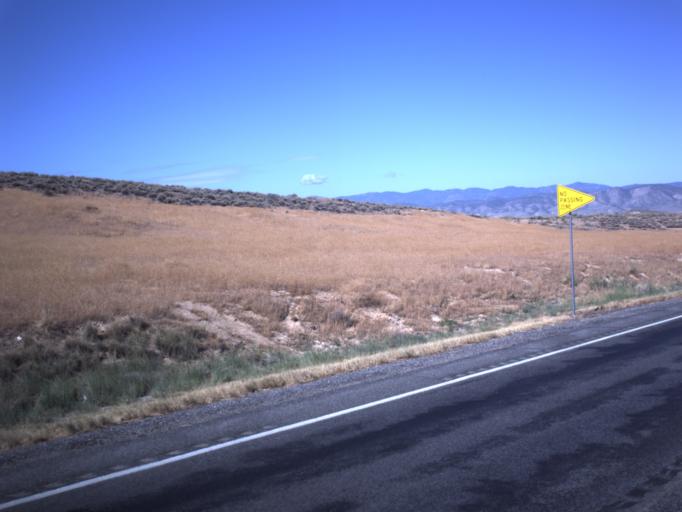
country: US
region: Utah
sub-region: Sanpete County
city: Gunnison
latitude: 39.1609
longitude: -111.7879
